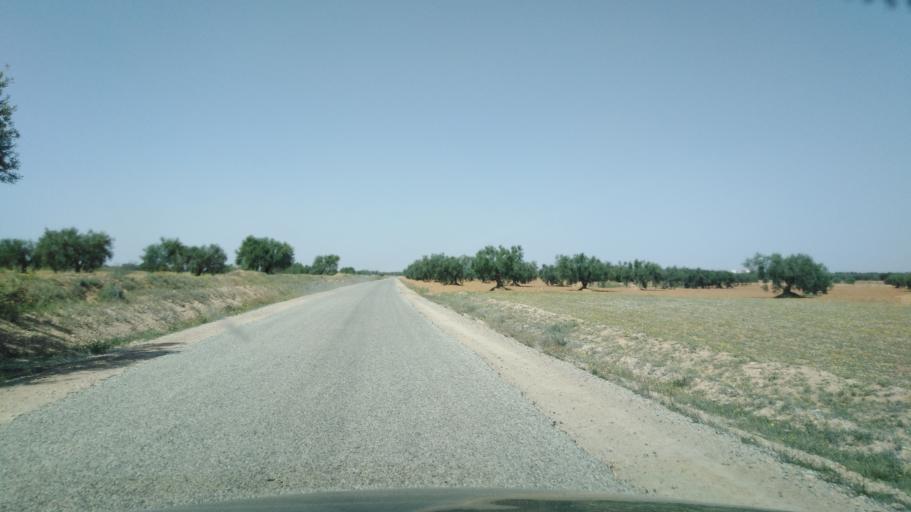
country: TN
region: Safaqis
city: Bi'r `Ali Bin Khalifah
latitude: 34.6782
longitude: 10.4014
